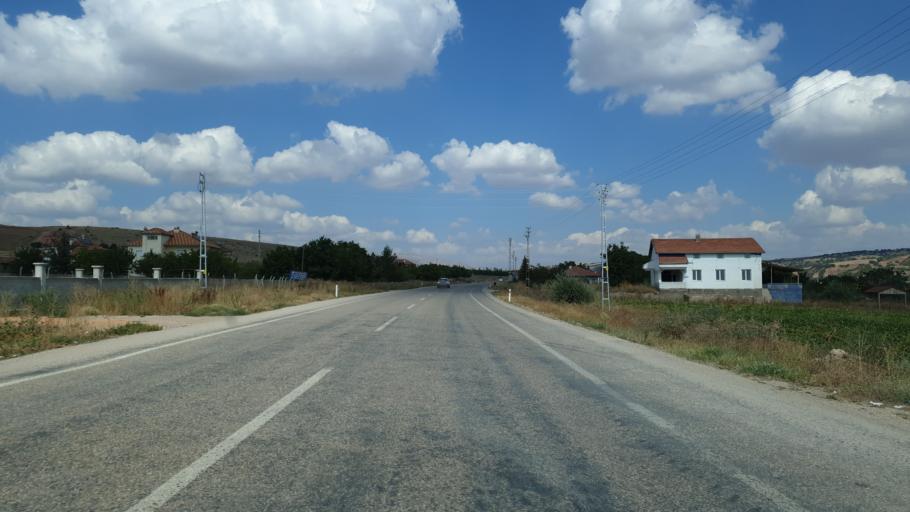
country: TR
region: Kayseri
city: Felahiye
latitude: 39.1006
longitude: 35.5869
